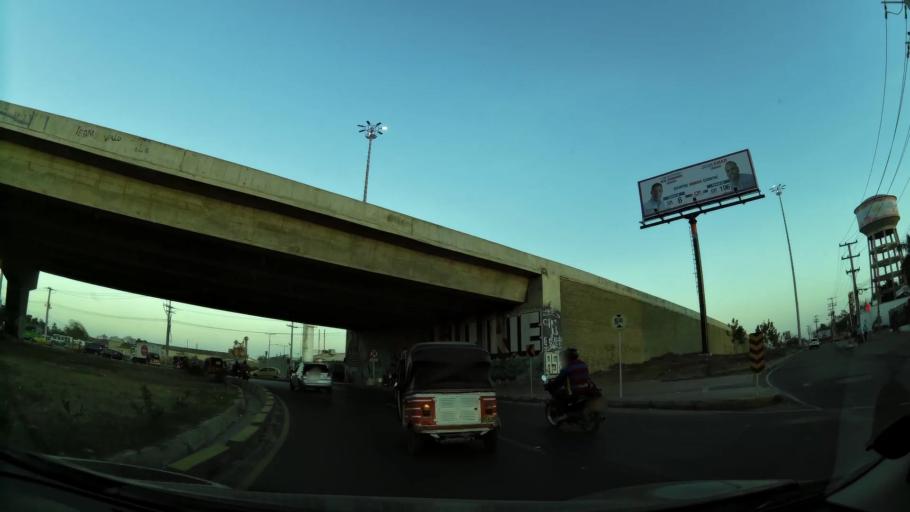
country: CO
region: Atlantico
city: Soledad
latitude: 10.9266
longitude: -74.7788
